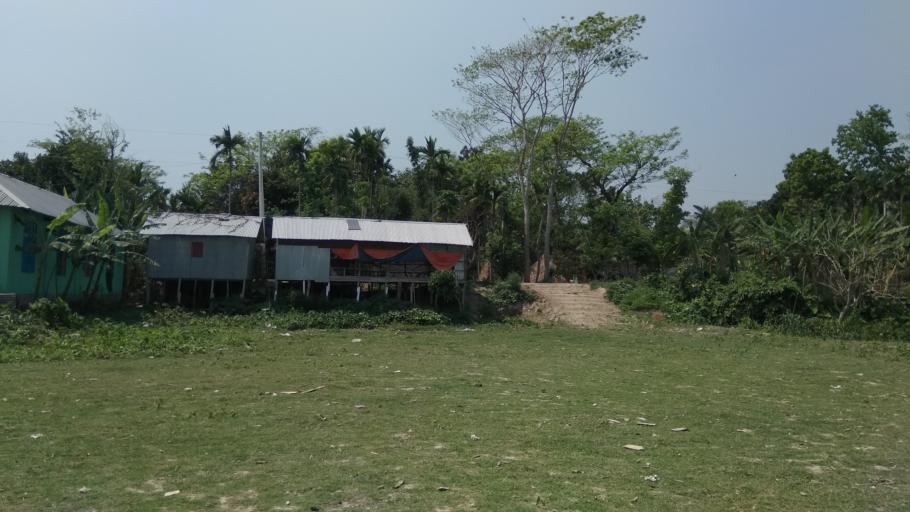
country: BD
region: Barisal
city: Mehendiganj
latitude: 22.9230
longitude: 90.3928
